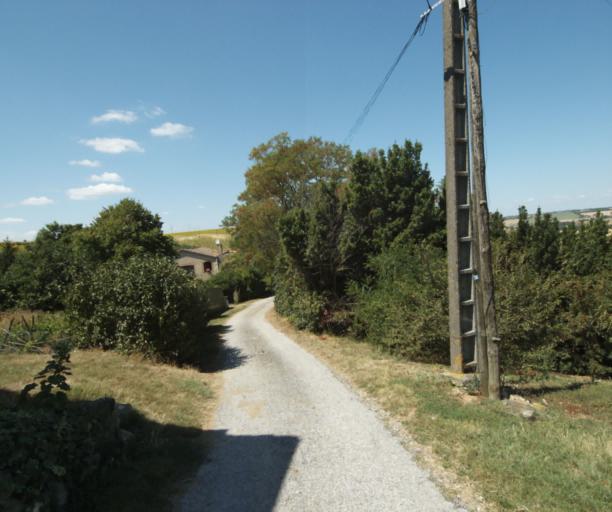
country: FR
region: Midi-Pyrenees
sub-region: Departement de la Haute-Garonne
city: Saint-Felix-Lauragais
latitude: 43.4654
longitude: 1.8778
